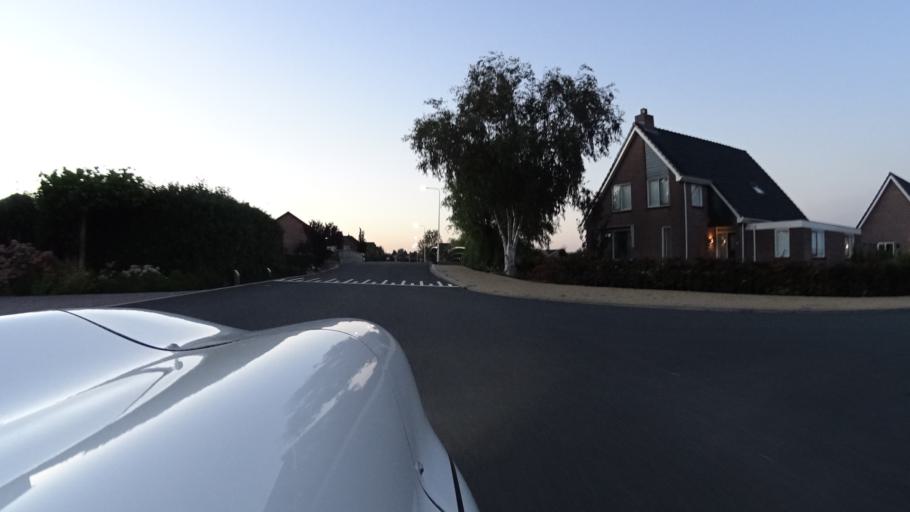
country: NL
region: South Holland
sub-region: Gemeente Kaag en Braassem
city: Oude Wetering
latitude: 52.1948
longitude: 4.6202
